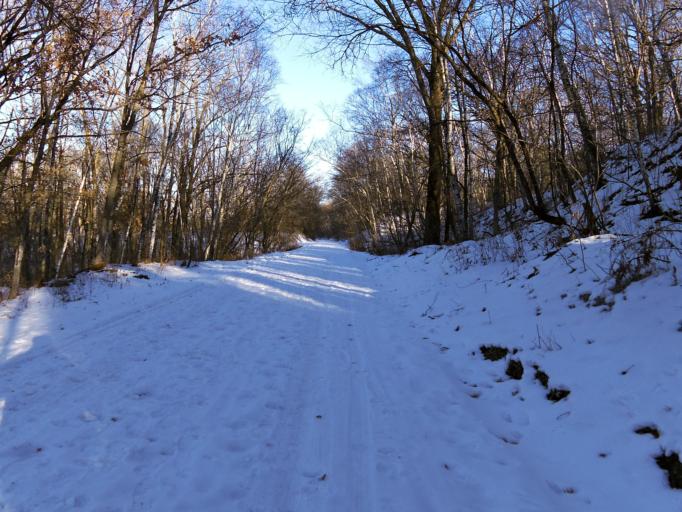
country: US
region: Minnesota
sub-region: Washington County
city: Grant
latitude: 45.0777
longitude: -92.8931
